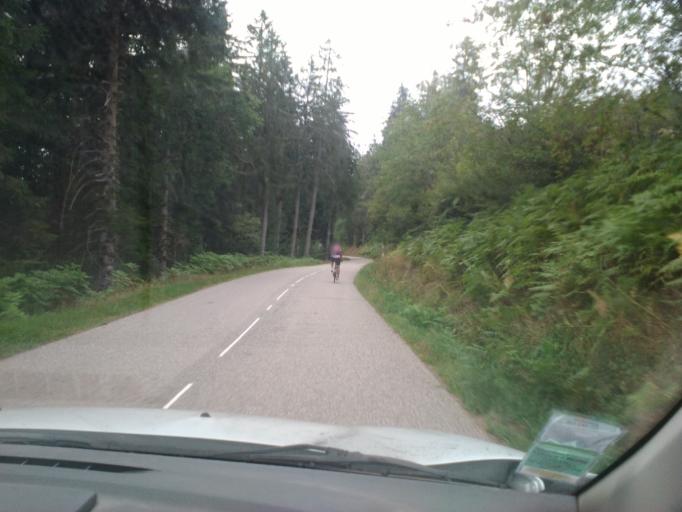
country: FR
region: Lorraine
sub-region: Departement des Vosges
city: Le Tholy
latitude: 48.1072
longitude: 6.7565
